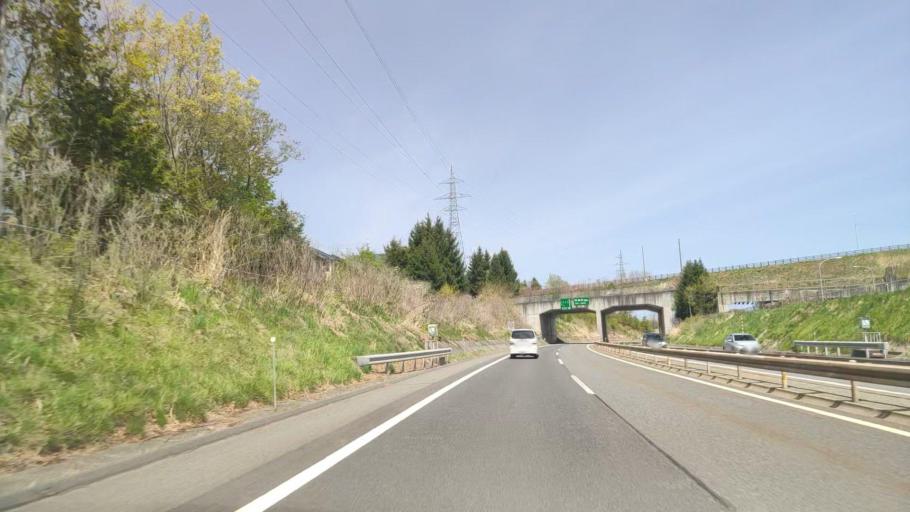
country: JP
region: Aomori
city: Hachinohe
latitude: 40.4774
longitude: 141.4595
